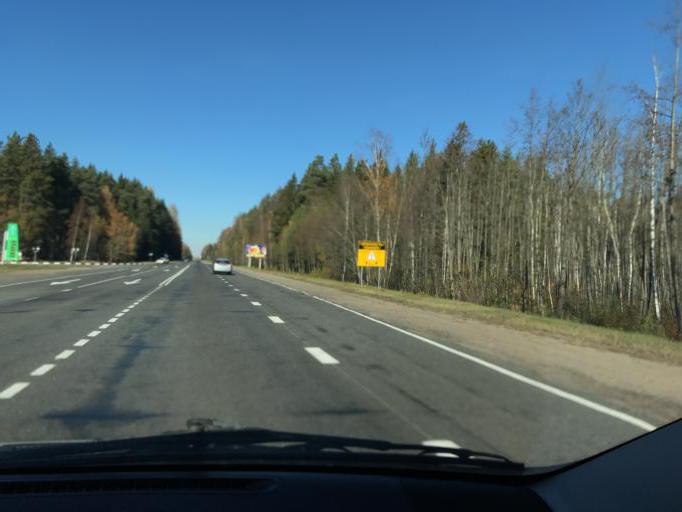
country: BY
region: Vitebsk
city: Polatsk
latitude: 55.4348
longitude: 28.7806
